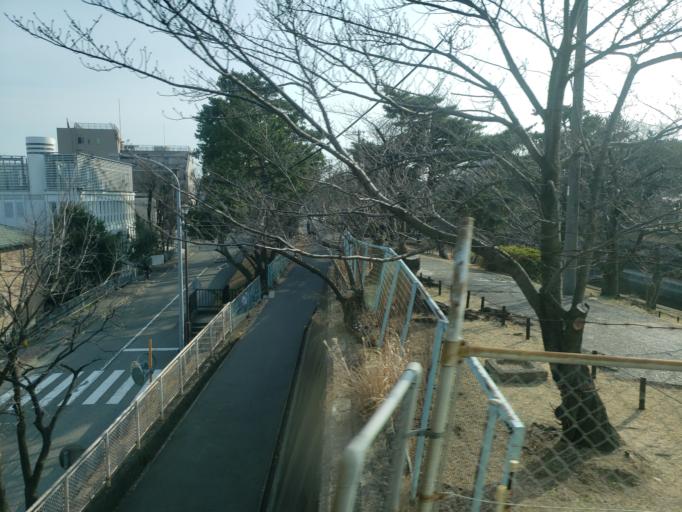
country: JP
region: Hyogo
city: Nishinomiya-hama
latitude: 34.7388
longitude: 135.3290
